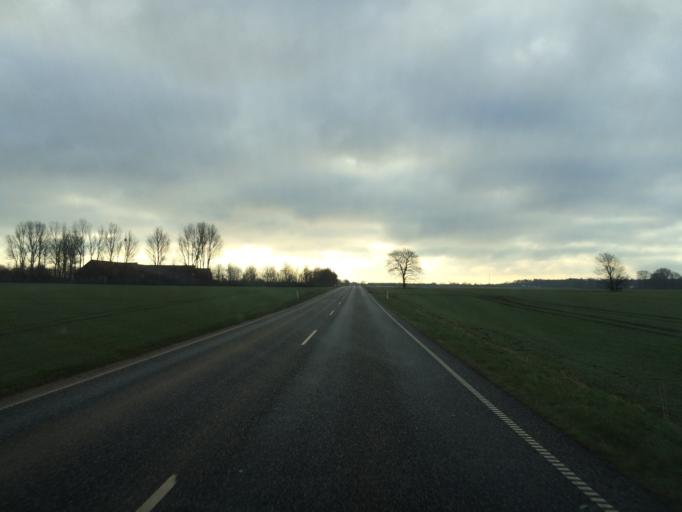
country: DK
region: South Denmark
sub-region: Fredericia Kommune
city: Taulov
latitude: 55.5699
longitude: 9.6737
